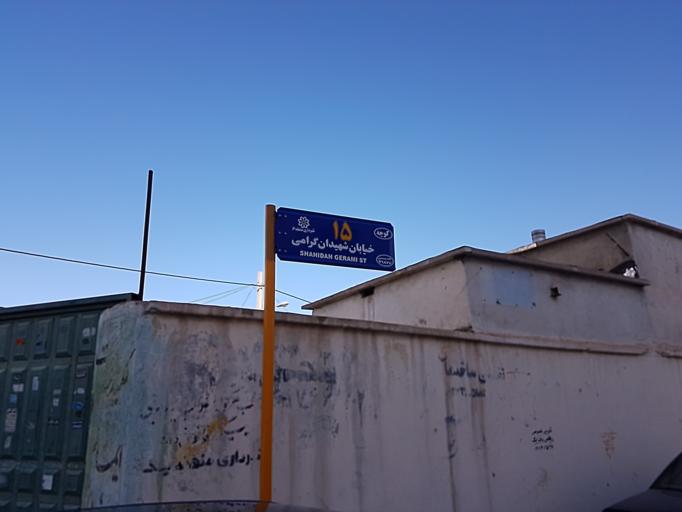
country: IR
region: Fars
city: Shiraz
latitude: 29.6719
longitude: 52.4599
